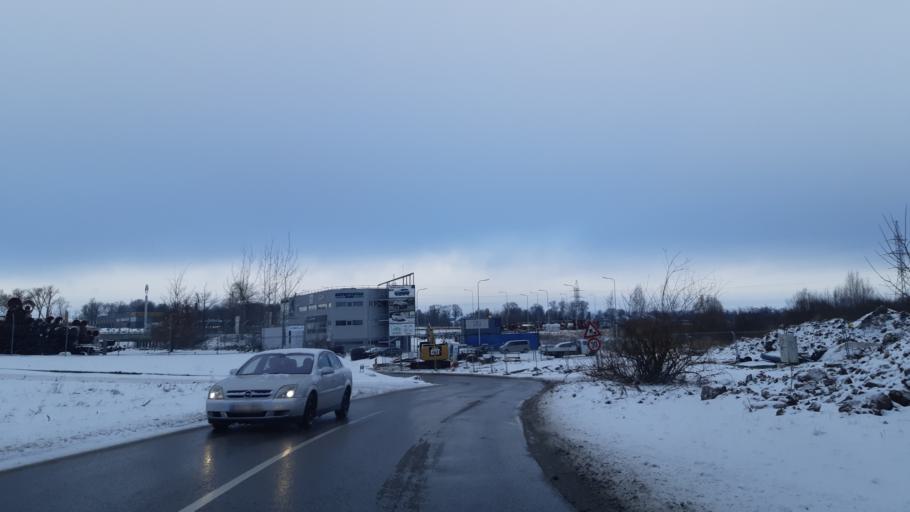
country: LT
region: Kauno apskritis
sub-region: Kaunas
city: Silainiai
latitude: 54.9350
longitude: 23.8751
